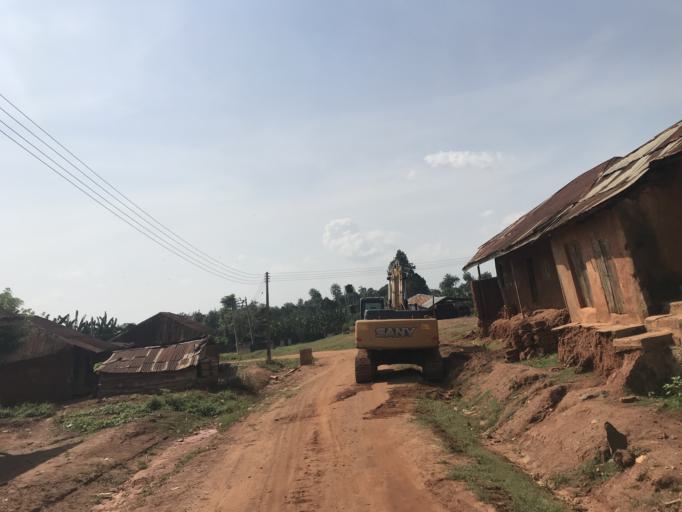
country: NG
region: Osun
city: Ilesa
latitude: 7.6355
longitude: 4.6721
